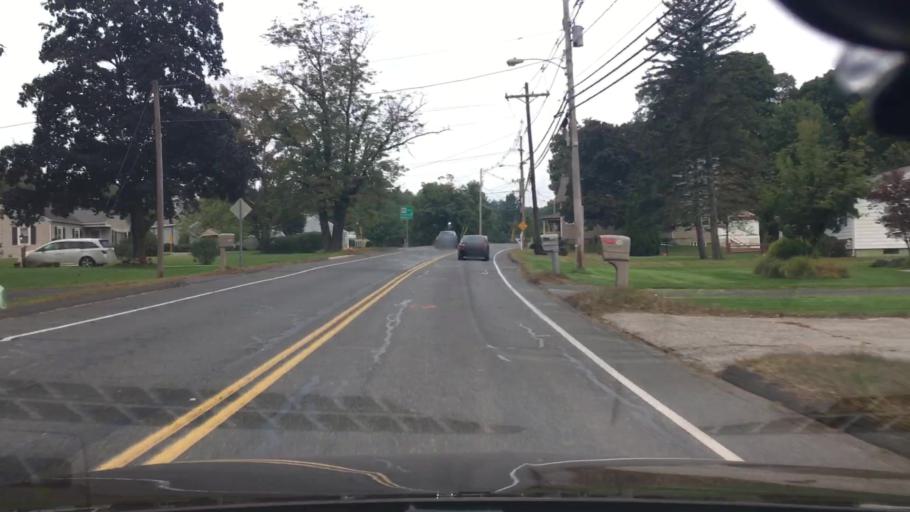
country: US
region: Massachusetts
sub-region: Hampden County
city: East Longmeadow
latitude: 42.0559
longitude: -72.4993
